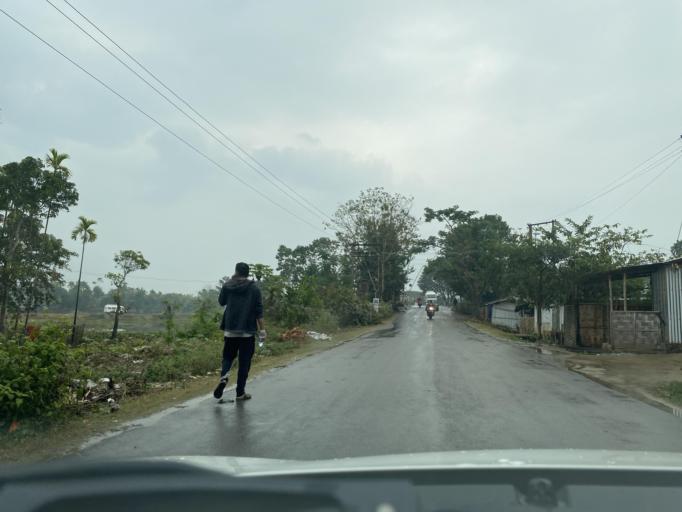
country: IN
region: Assam
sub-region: Cachar
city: Lakhipur
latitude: 24.8297
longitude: 93.0270
